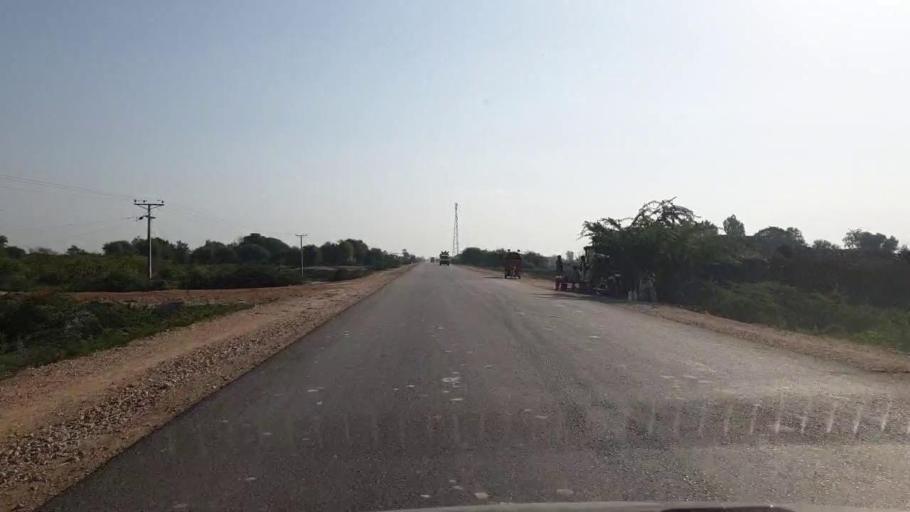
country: PK
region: Sindh
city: Badin
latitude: 24.6585
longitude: 68.9473
